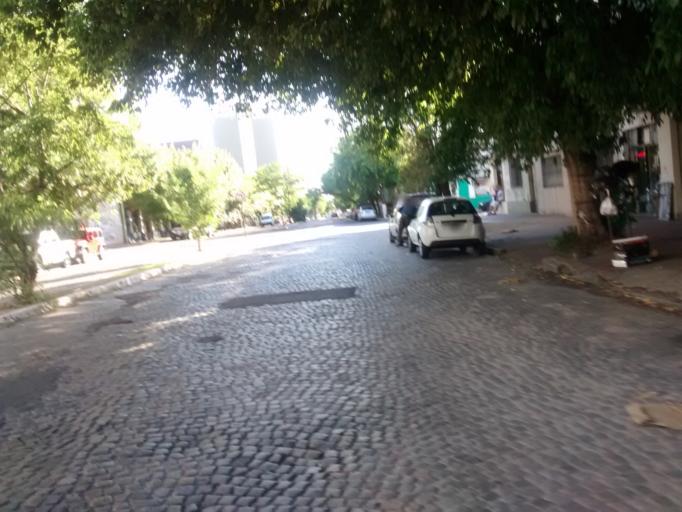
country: AR
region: Buenos Aires
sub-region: Partido de La Plata
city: La Plata
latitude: -34.9273
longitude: -57.9484
